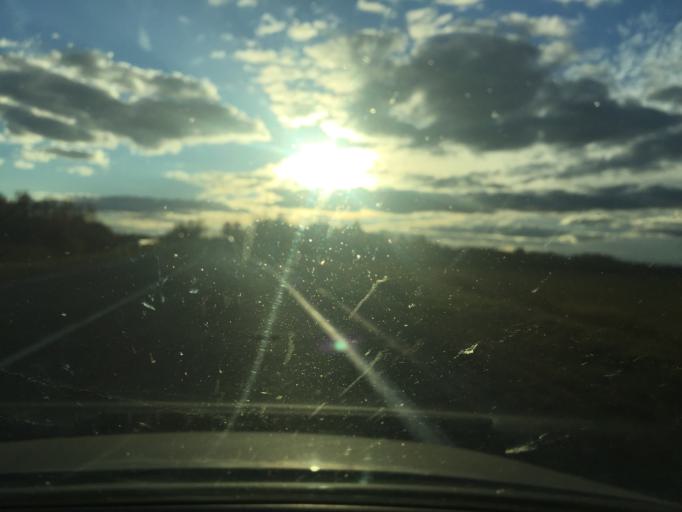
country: BY
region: Vitebsk
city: Vyerkhnyadzvinsk
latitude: 55.8347
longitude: 27.8252
